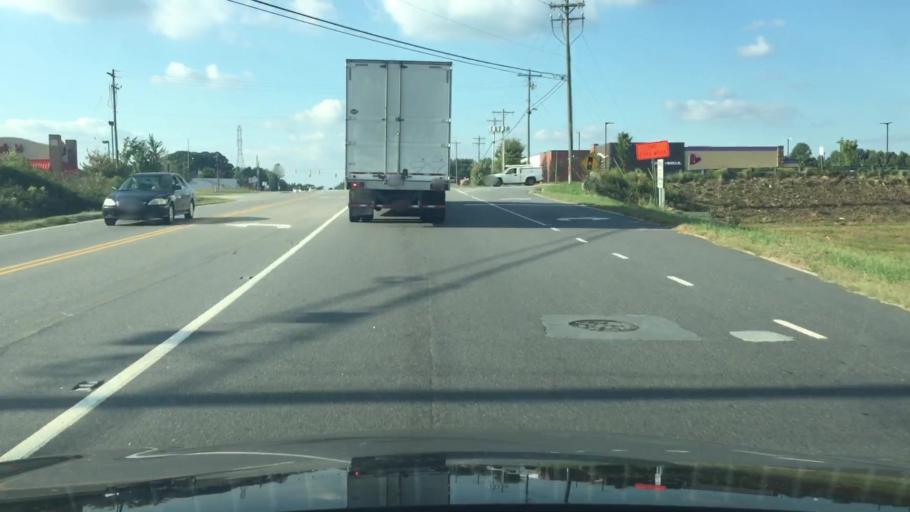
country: US
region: North Carolina
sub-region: Iredell County
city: Troutman
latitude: 35.6688
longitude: -80.8529
